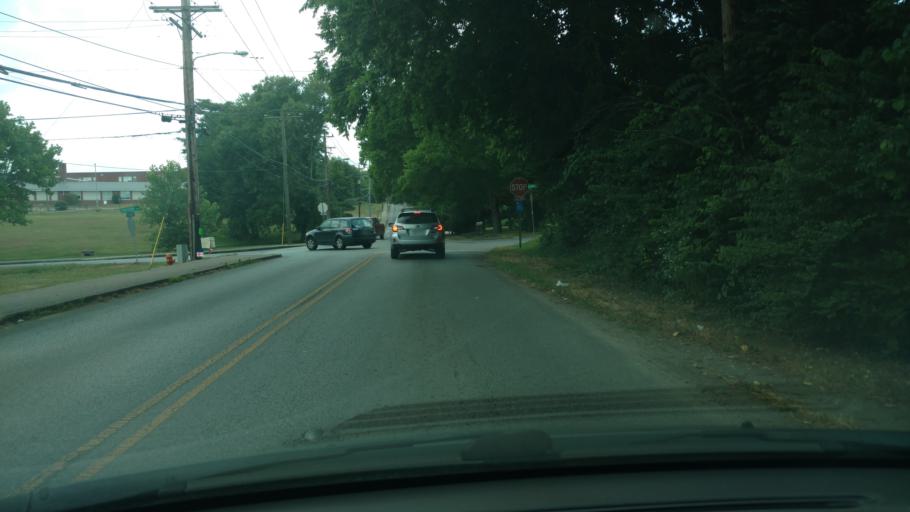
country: US
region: Tennessee
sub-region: Davidson County
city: Nashville
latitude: 36.2081
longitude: -86.7167
